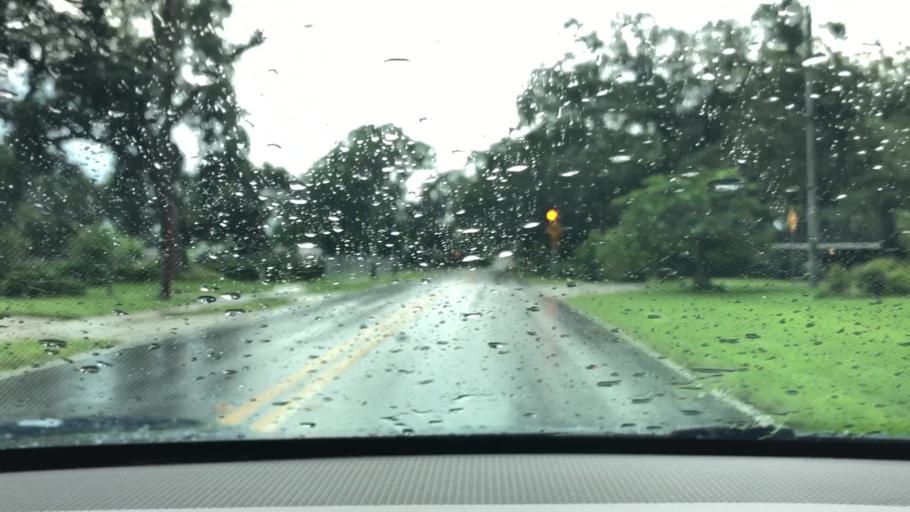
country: US
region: Florida
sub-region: Orange County
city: Edgewood
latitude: 28.4949
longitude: -81.3526
